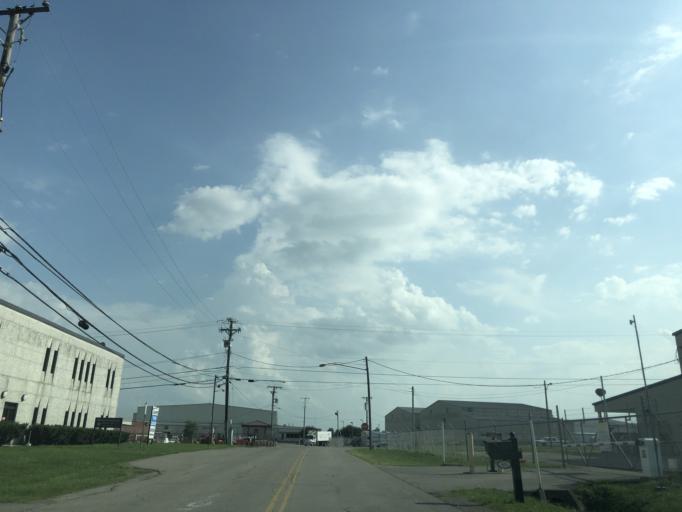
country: US
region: Tennessee
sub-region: Davidson County
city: Oak Hill
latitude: 36.1142
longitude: -86.6780
